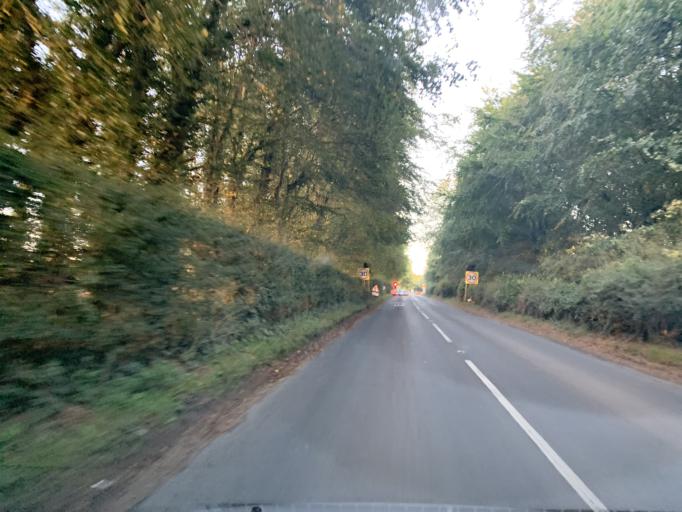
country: GB
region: England
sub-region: Wiltshire
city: Woodford
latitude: 51.0984
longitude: -1.8416
